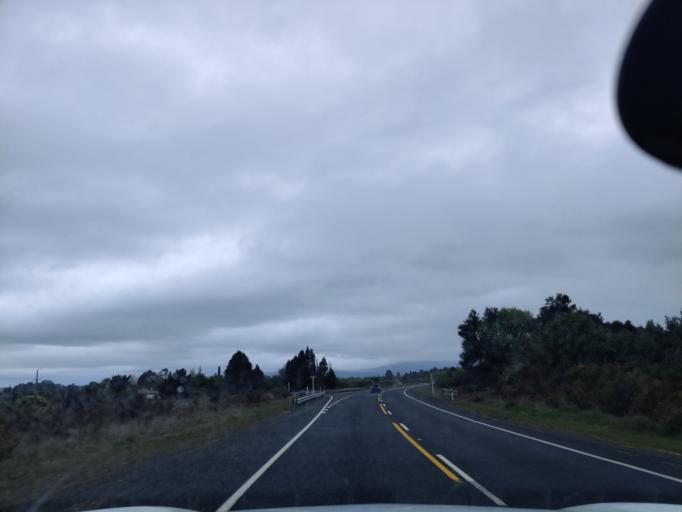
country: NZ
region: Waikato
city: Turangi
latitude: -38.9798
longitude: 175.7768
